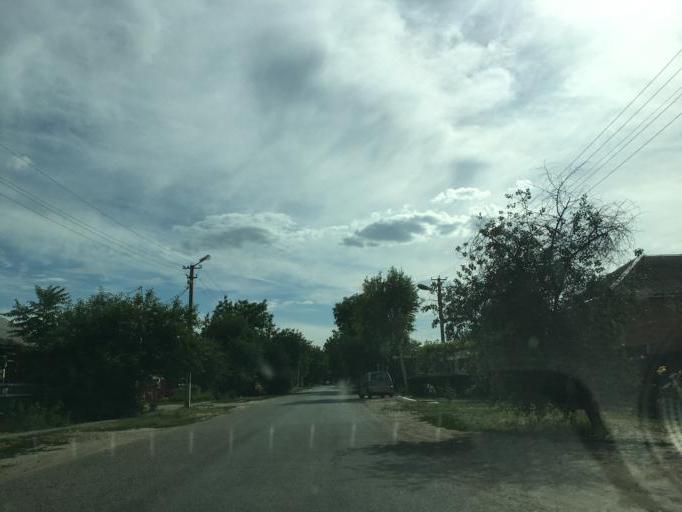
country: RU
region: Krasnodarskiy
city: Kushchevskaya
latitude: 46.5512
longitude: 39.6214
